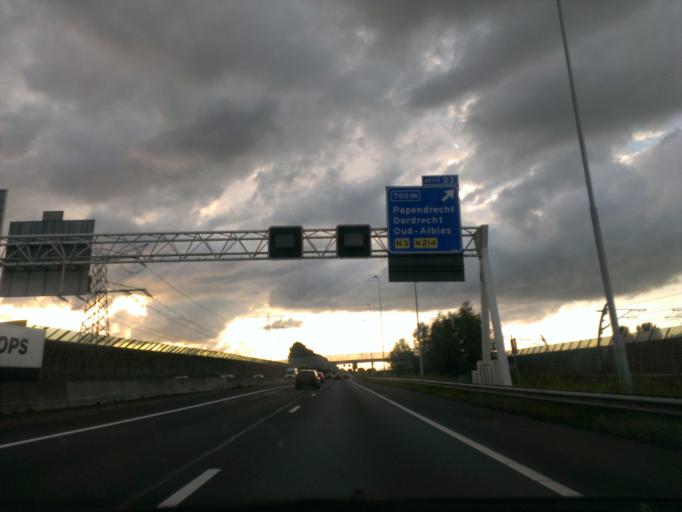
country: NL
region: South Holland
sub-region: Gemeente Sliedrecht
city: Sliedrecht
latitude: 51.8340
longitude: 4.7351
